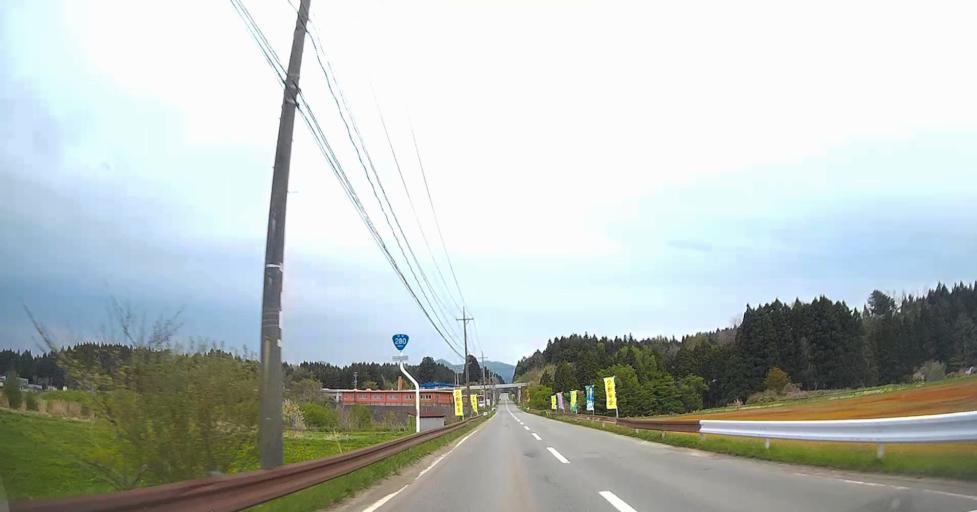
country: JP
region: Aomori
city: Goshogawara
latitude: 41.1780
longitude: 140.4770
